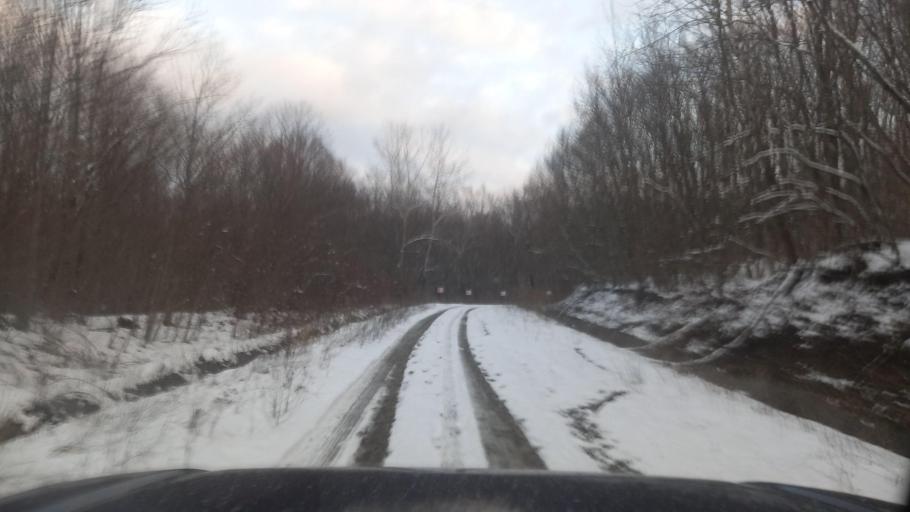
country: RU
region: Krasnodarskiy
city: Smolenskaya
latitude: 44.6746
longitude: 38.7843
